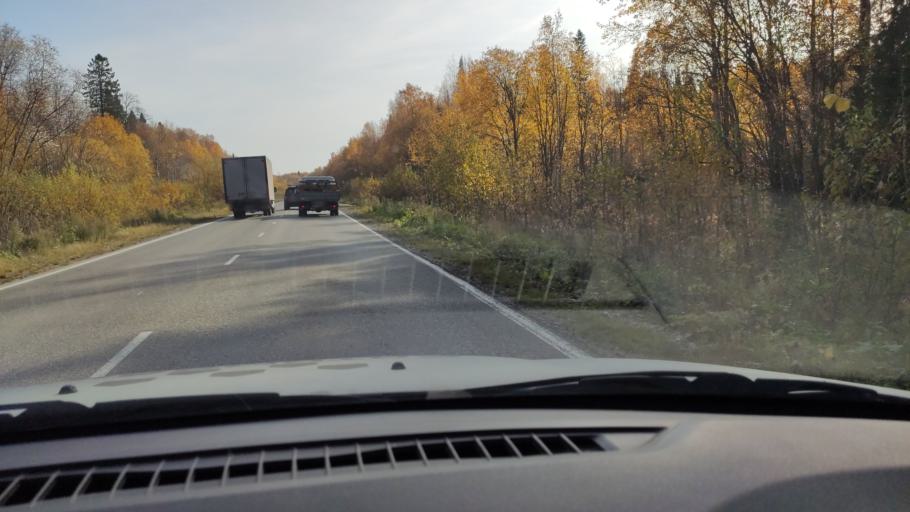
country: RU
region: Perm
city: Novyye Lyady
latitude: 58.0243
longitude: 56.6371
